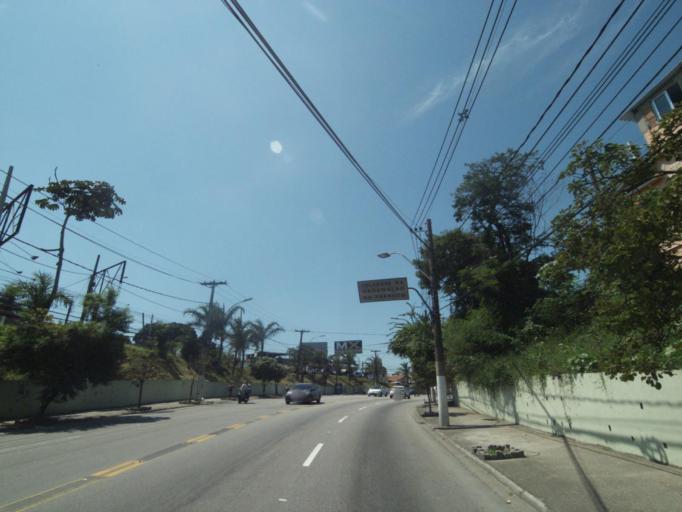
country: BR
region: Rio de Janeiro
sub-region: Niteroi
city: Niteroi
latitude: -22.9090
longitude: -43.0691
